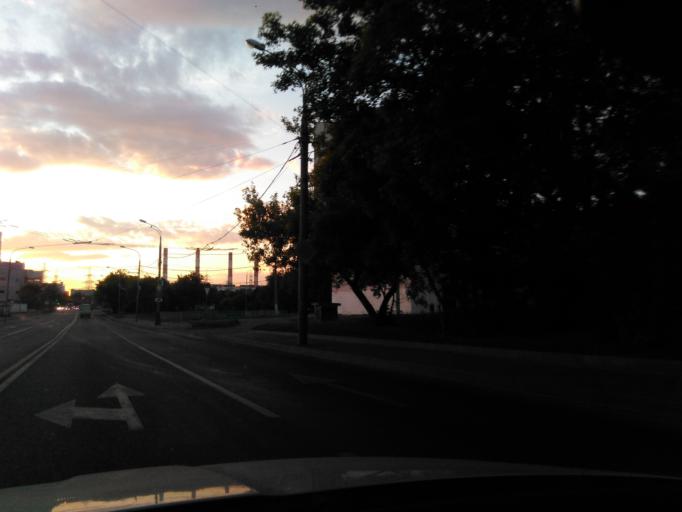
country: RU
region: Moscow
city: Businovo
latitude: 55.8847
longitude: 37.5165
